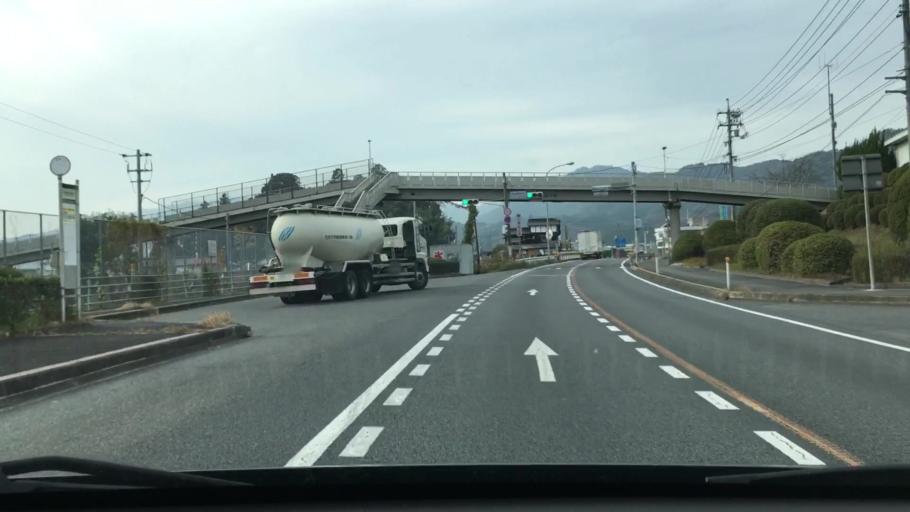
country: JP
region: Yamaguchi
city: Yanai
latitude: 34.0919
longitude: 132.0569
